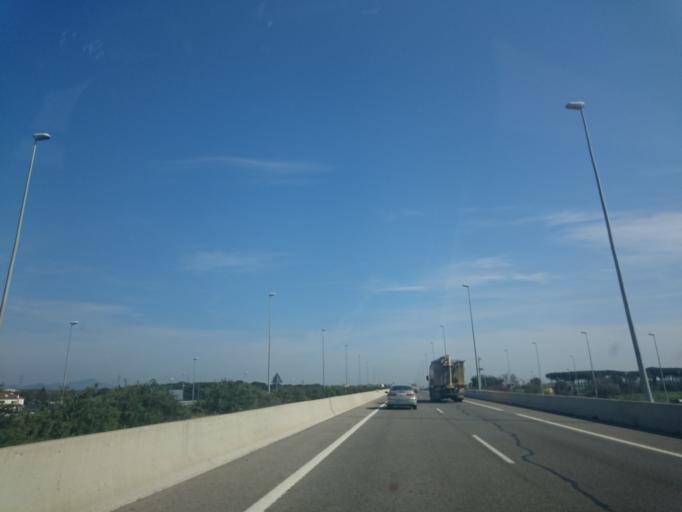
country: ES
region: Catalonia
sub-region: Provincia de Girona
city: Riudellots de la Selva
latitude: 41.8887
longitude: 2.7829
